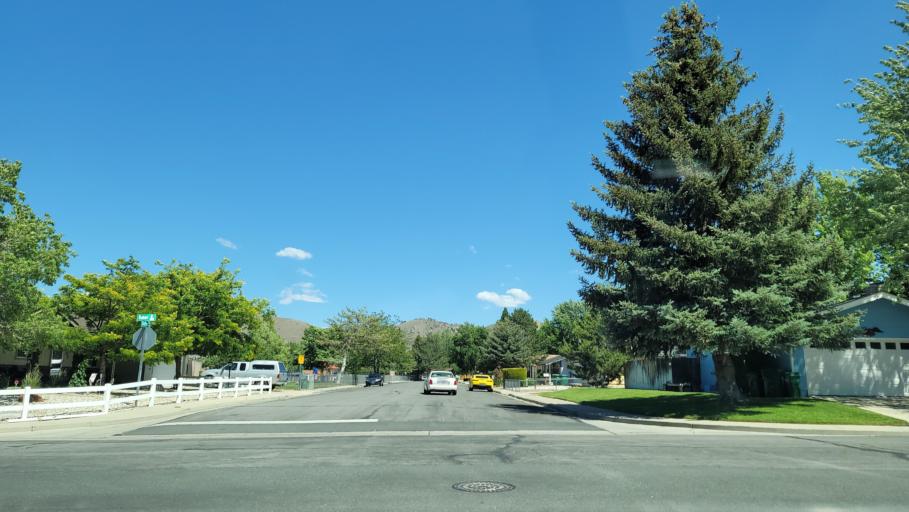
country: US
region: Nevada
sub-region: Carson City
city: Carson City
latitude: 39.1395
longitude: -119.7593
